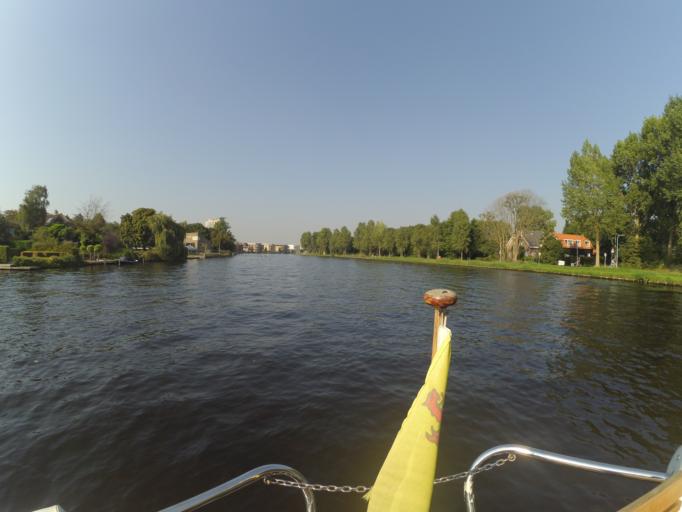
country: NL
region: North Holland
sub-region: Gemeente Haarlem
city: Haarlem
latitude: 52.3654
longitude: 4.6370
